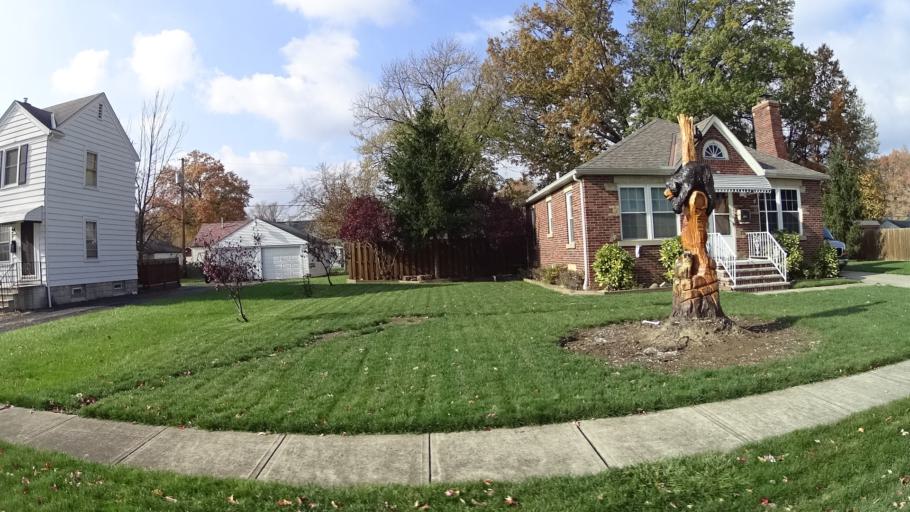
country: US
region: Ohio
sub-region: Lorain County
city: Elyria
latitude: 41.3680
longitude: -82.0817
